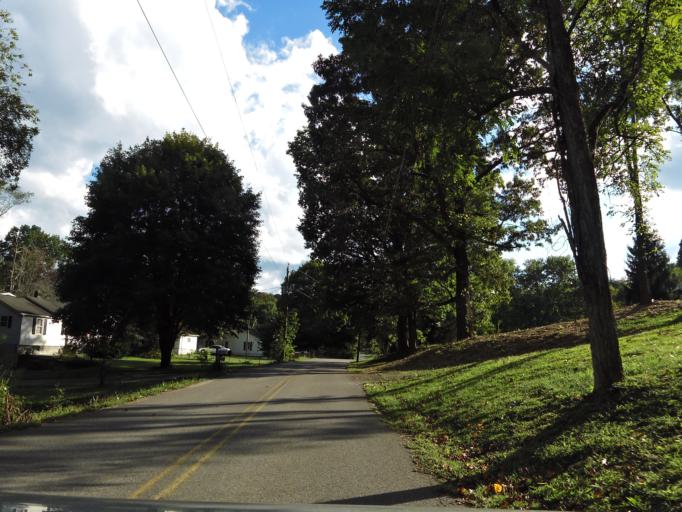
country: US
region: Tennessee
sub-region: Knox County
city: Mascot
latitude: 36.1155
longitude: -83.7498
